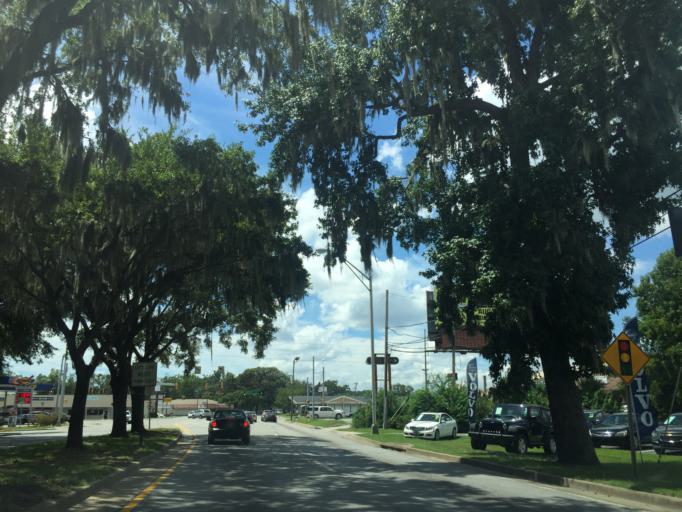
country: US
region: Georgia
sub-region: Chatham County
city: Montgomery
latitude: 31.9995
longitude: -81.1219
